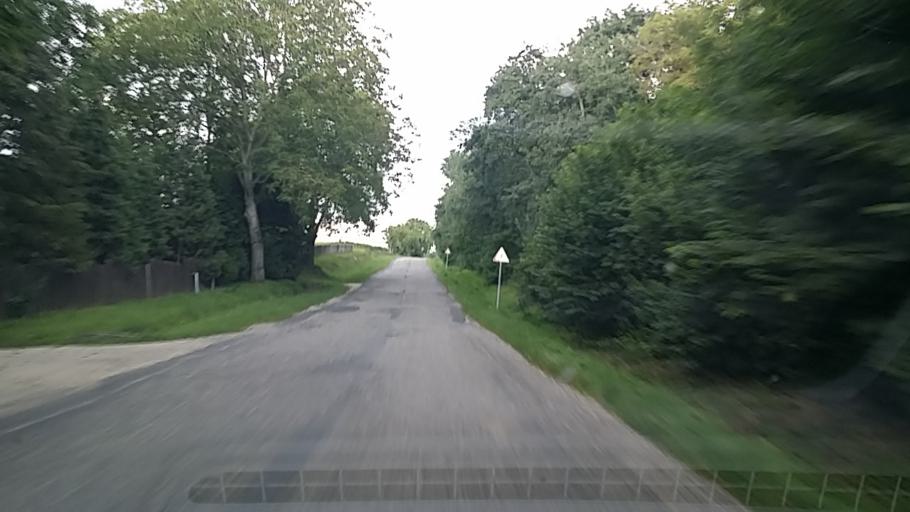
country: HU
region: Zala
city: Nagykanizsa
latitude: 46.5013
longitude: 17.0812
